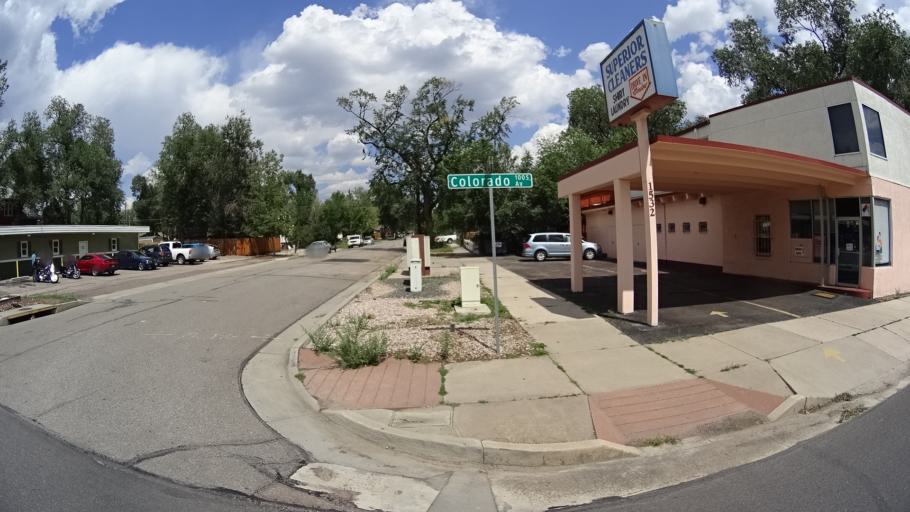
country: US
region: Colorado
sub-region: El Paso County
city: Colorado Springs
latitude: 38.8395
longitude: -104.8495
